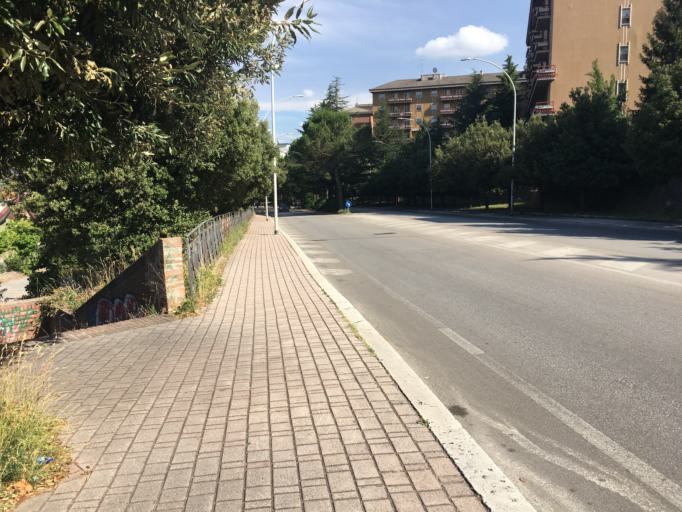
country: IT
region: Molise
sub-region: Provincia di Campobasso
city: Campobasso
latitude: 41.5544
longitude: 14.6616
